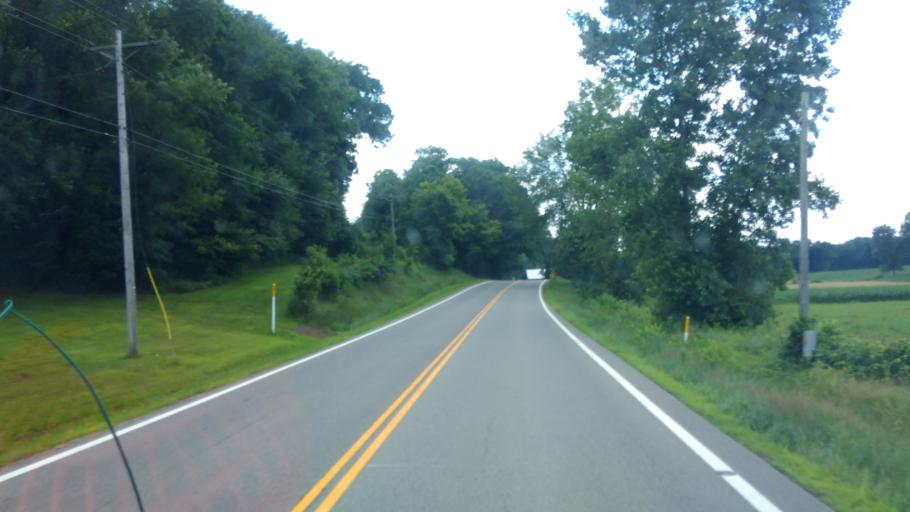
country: US
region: Ohio
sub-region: Ashland County
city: Loudonville
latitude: 40.7007
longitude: -82.3322
